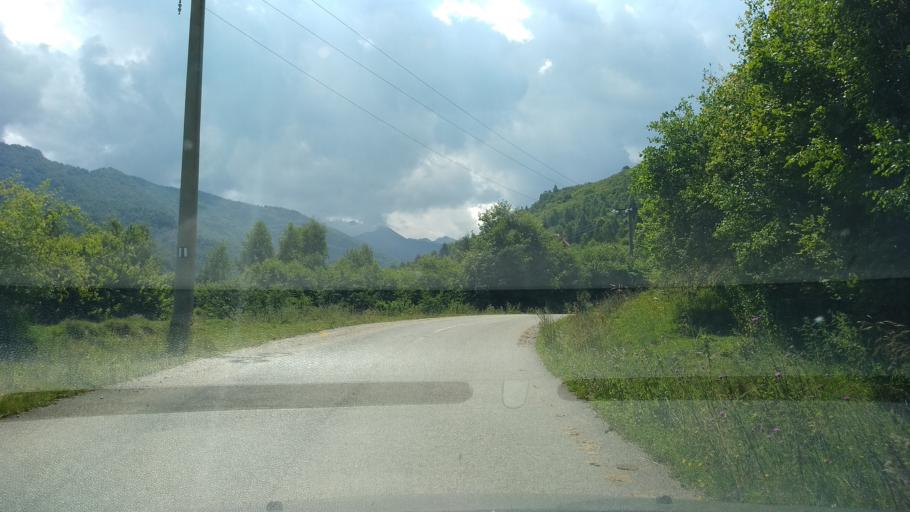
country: RO
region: Hunedoara
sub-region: Comuna Rau de Mori
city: Rau de Mori
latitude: 45.4659
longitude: 22.8960
